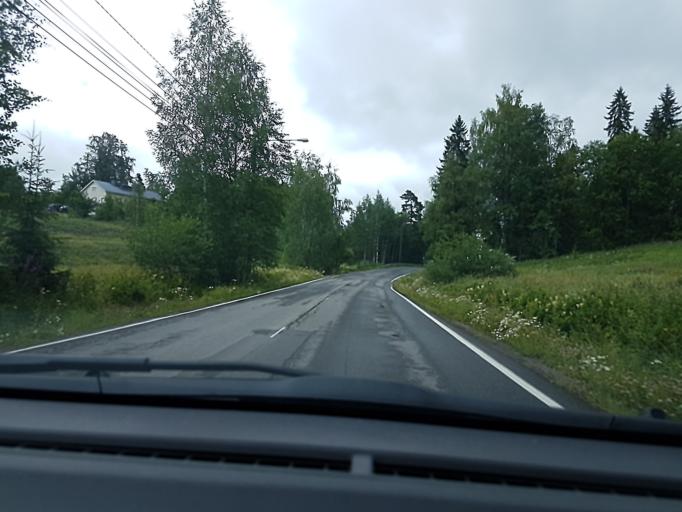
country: FI
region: Uusimaa
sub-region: Helsinki
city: Pornainen
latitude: 60.4372
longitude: 25.3830
